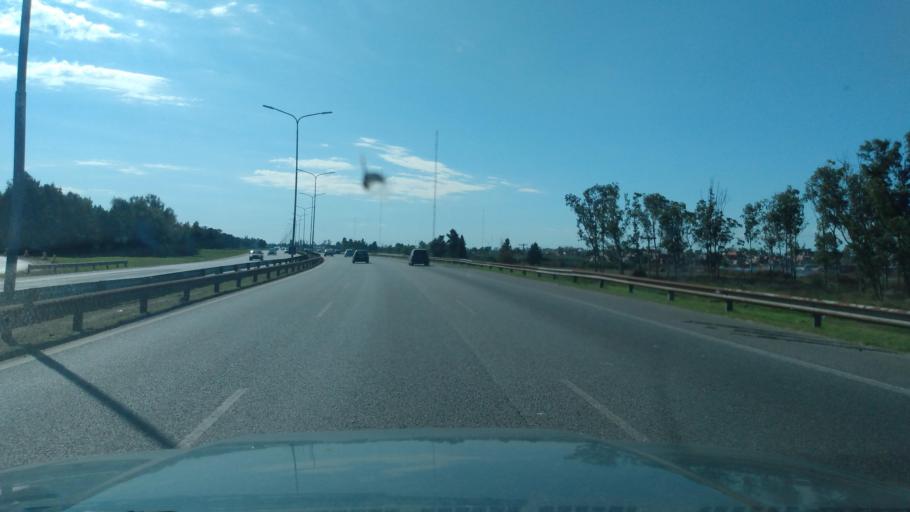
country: AR
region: Buenos Aires
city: Hurlingham
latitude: -34.5475
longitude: -58.6050
